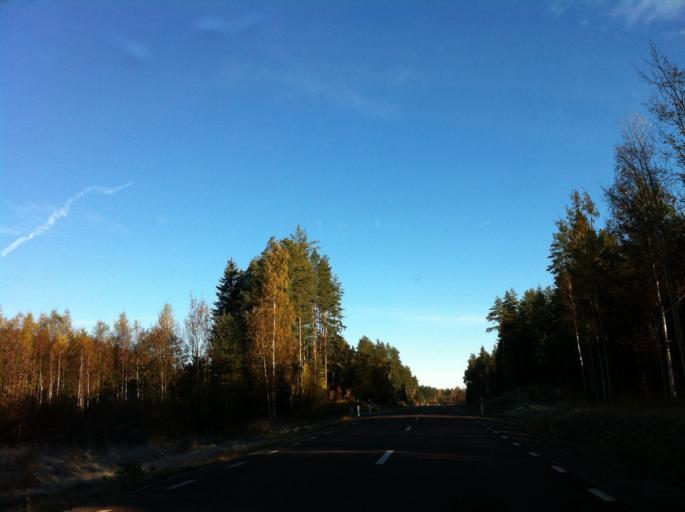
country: SE
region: Gaevleborg
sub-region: Gavle Kommun
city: Gavle
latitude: 60.5610
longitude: 17.1248
